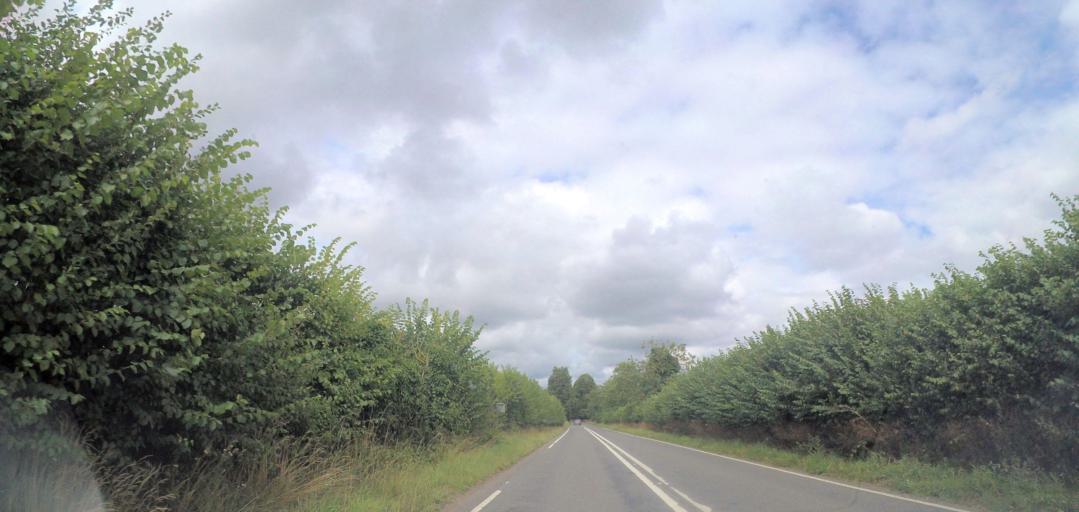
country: GB
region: England
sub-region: Suffolk
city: Lakenheath
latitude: 52.3312
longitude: 0.5192
